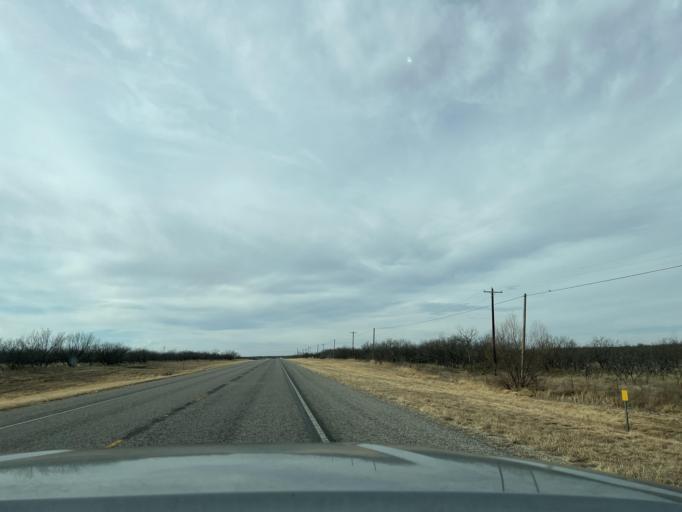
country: US
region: Texas
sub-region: Shackelford County
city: Albany
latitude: 32.7580
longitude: -99.5645
